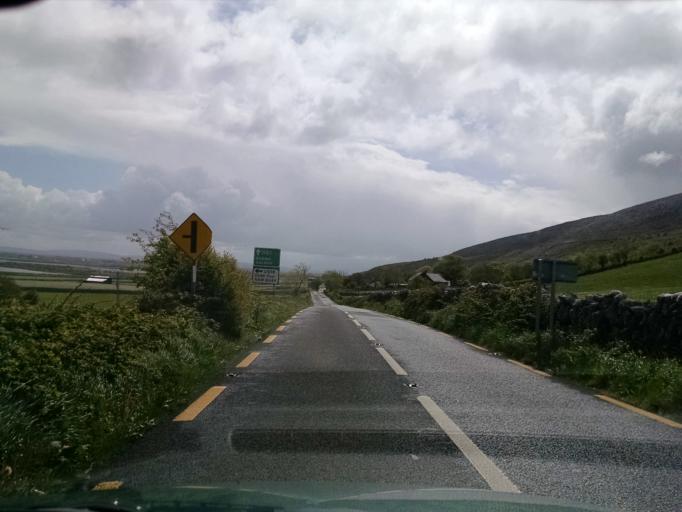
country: IE
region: Connaught
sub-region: County Galway
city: Gaillimh
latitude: 53.1497
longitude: -9.0550
